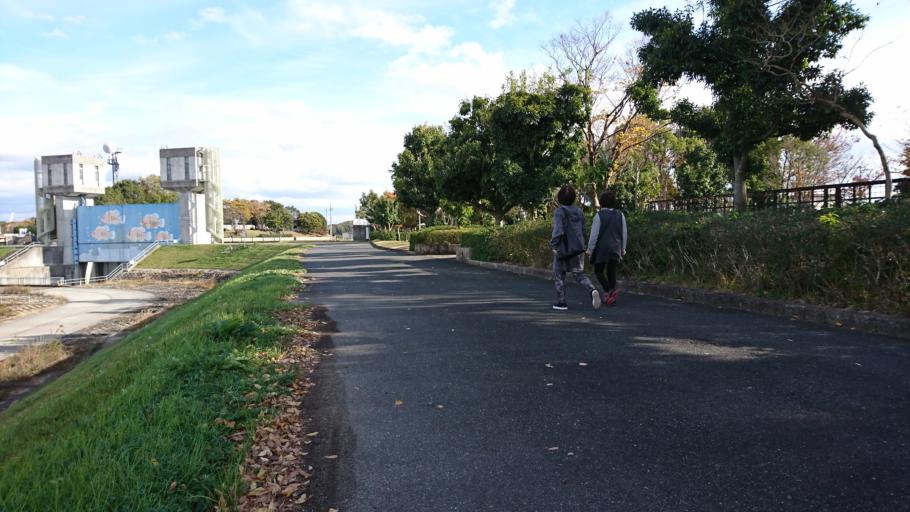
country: JP
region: Hyogo
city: Kakogawacho-honmachi
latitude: 34.7927
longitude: 134.8883
